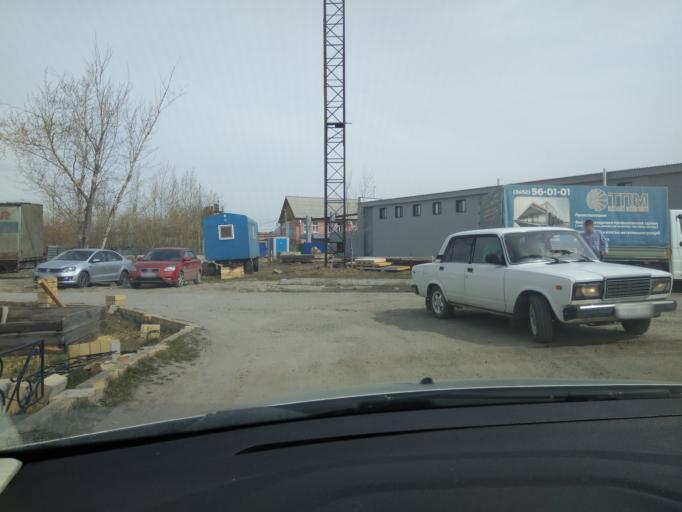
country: RU
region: Tjumen
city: Melioratorov
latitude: 57.1900
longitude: 65.5992
